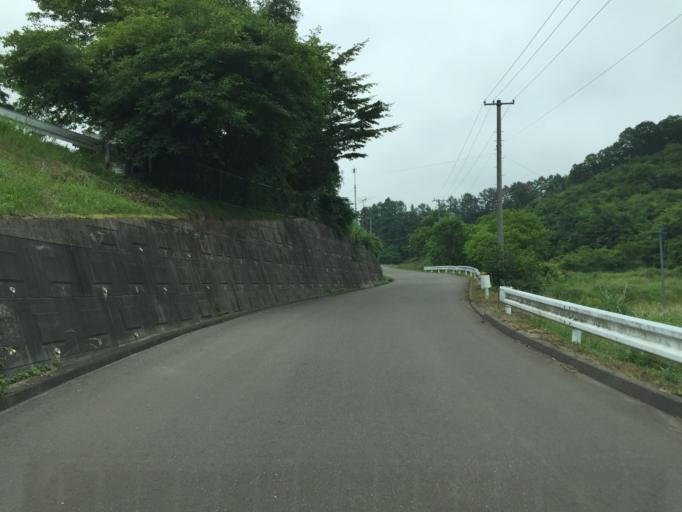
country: JP
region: Miyagi
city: Marumori
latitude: 37.7981
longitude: 140.7445
